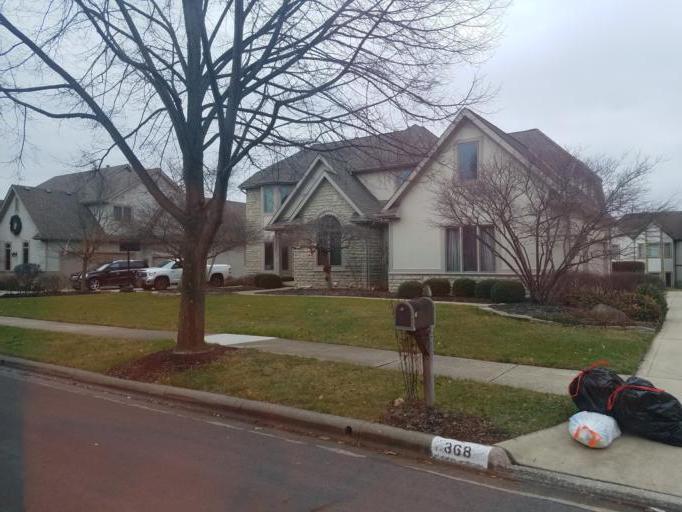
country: US
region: Ohio
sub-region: Franklin County
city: Westerville
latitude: 40.1357
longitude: -82.9574
